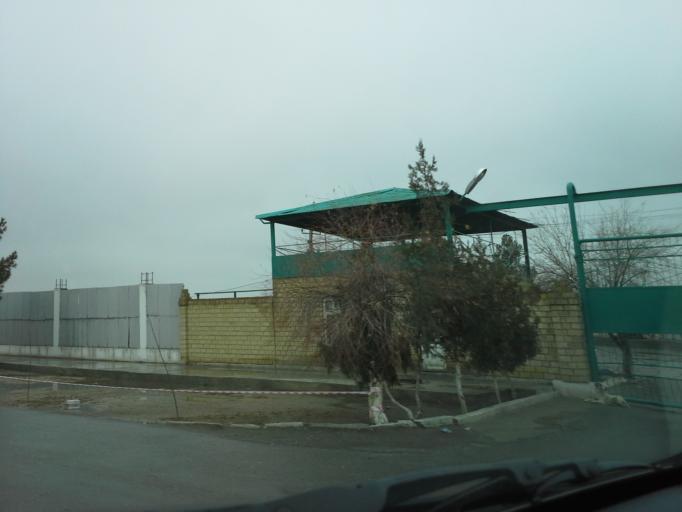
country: TM
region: Ahal
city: Ashgabat
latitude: 37.9474
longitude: 58.4301
